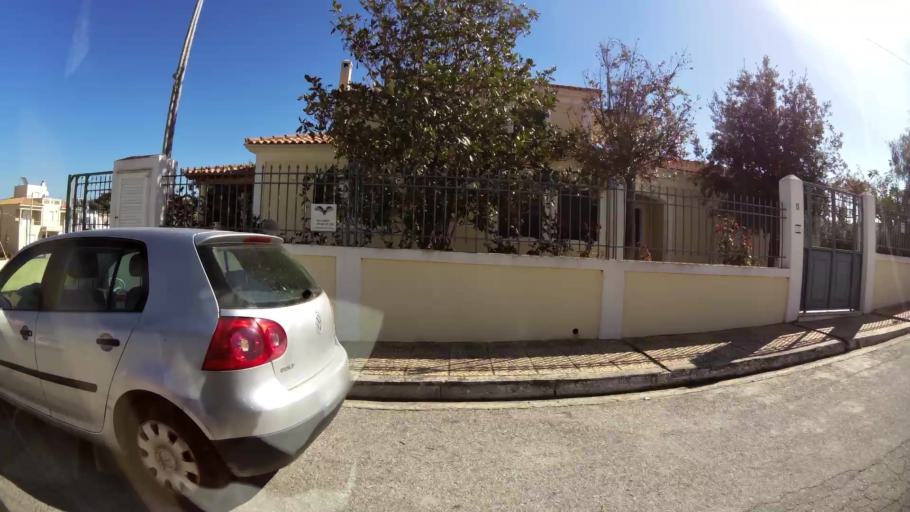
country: GR
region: Attica
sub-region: Nomarchia Anatolikis Attikis
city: Markopoulo
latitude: 37.8864
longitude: 23.9426
